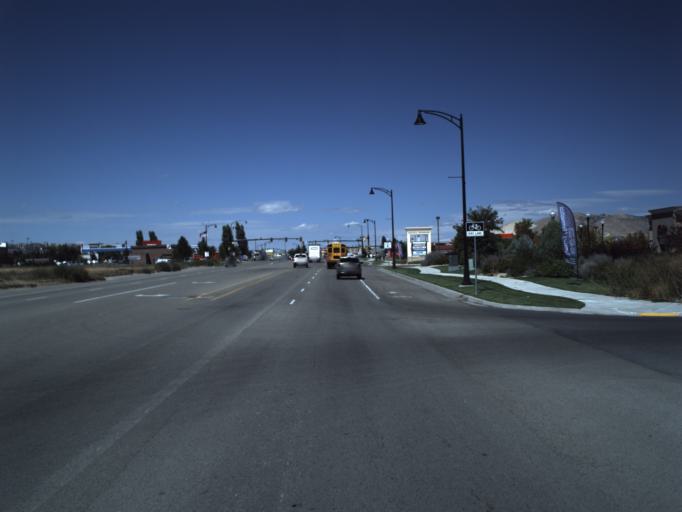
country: US
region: Utah
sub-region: Utah County
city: Saratoga Springs
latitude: 40.3847
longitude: -111.9163
